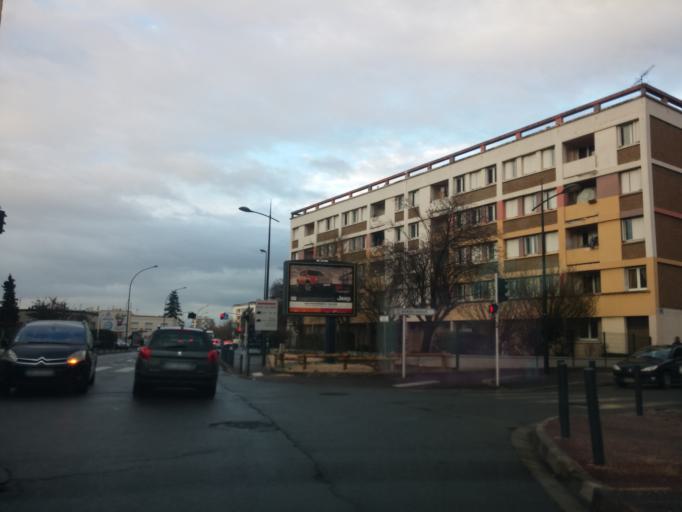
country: FR
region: Midi-Pyrenees
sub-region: Departement de la Haute-Garonne
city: Toulouse
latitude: 43.5702
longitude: 1.4162
